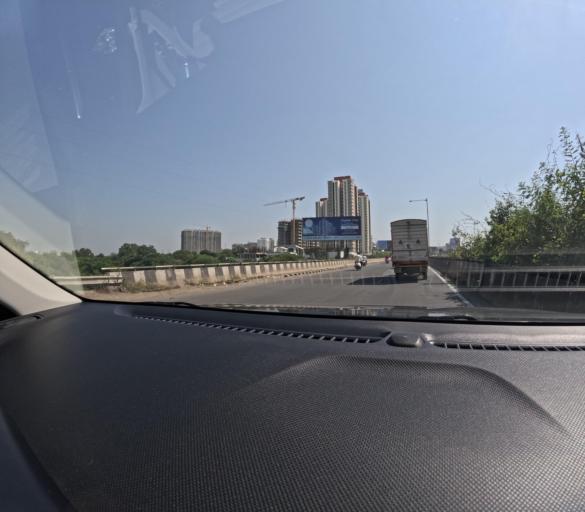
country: IN
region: Maharashtra
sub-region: Pune Division
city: Pimpri
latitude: 18.5875
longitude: 73.7589
